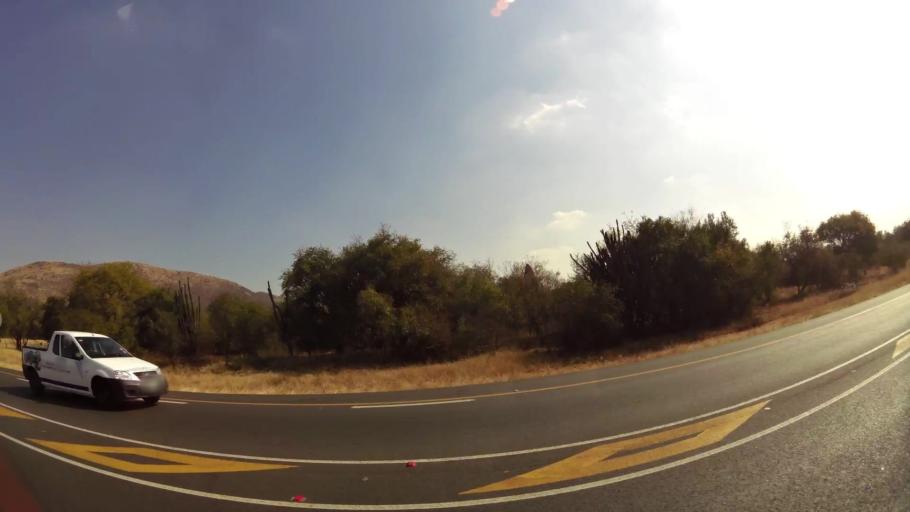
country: ZA
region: North-West
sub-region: Bojanala Platinum District Municipality
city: Rustenburg
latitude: -25.6328
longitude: 27.1574
